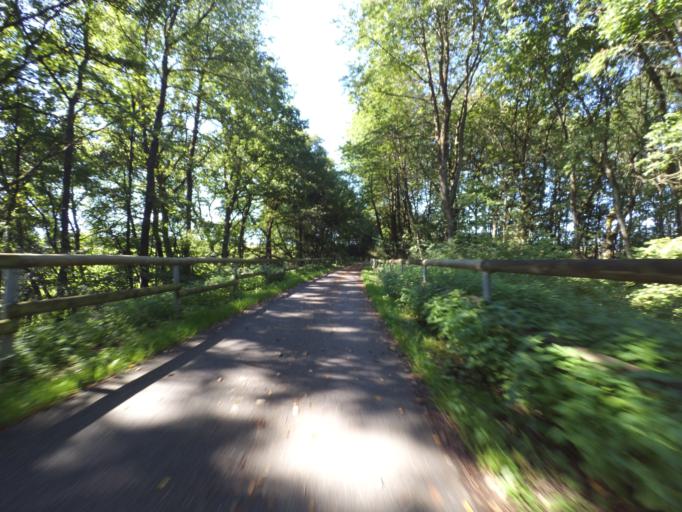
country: DE
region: Rheinland-Pfalz
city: Eckfeld
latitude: 50.1060
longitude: 6.8467
